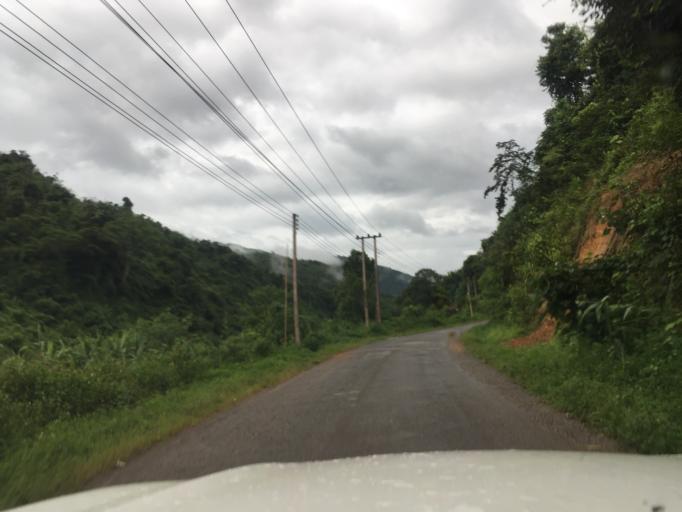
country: LA
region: Oudomxai
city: Muang La
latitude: 20.9847
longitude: 102.2255
